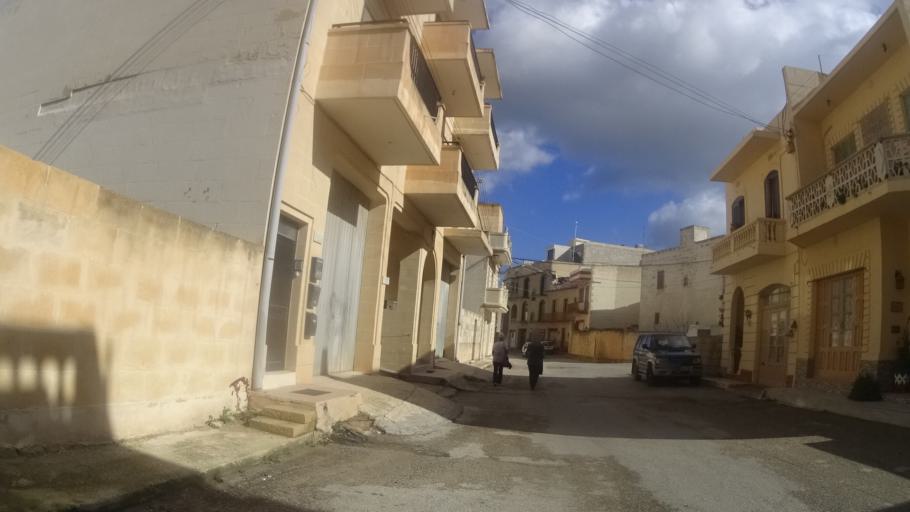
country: MT
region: In-Nadur
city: Nadur
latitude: 36.0377
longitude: 14.2873
